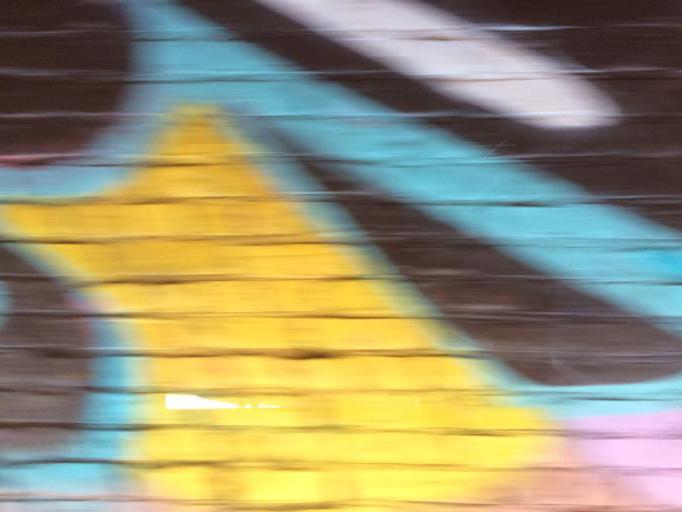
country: DE
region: North Rhine-Westphalia
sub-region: Regierungsbezirk Dusseldorf
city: Dusseldorf
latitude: 51.2244
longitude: 6.7994
